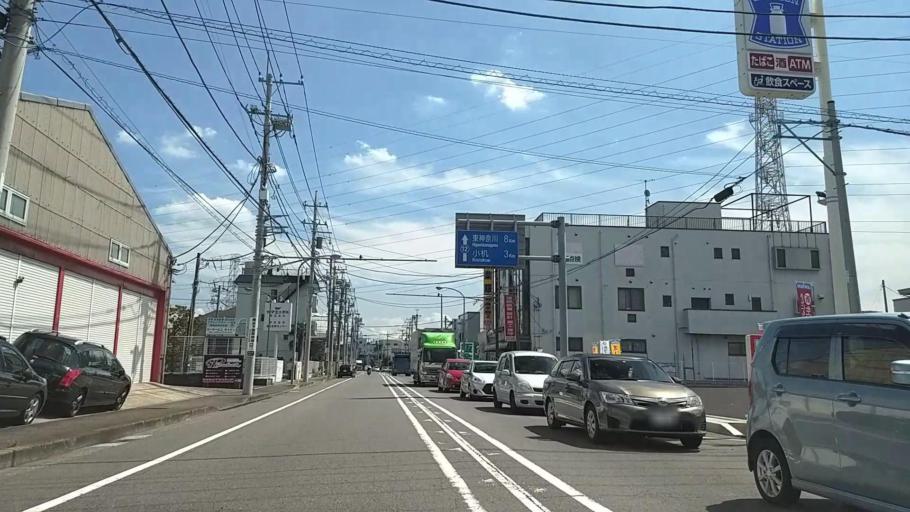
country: JP
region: Kanagawa
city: Yokohama
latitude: 35.5165
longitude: 139.5783
